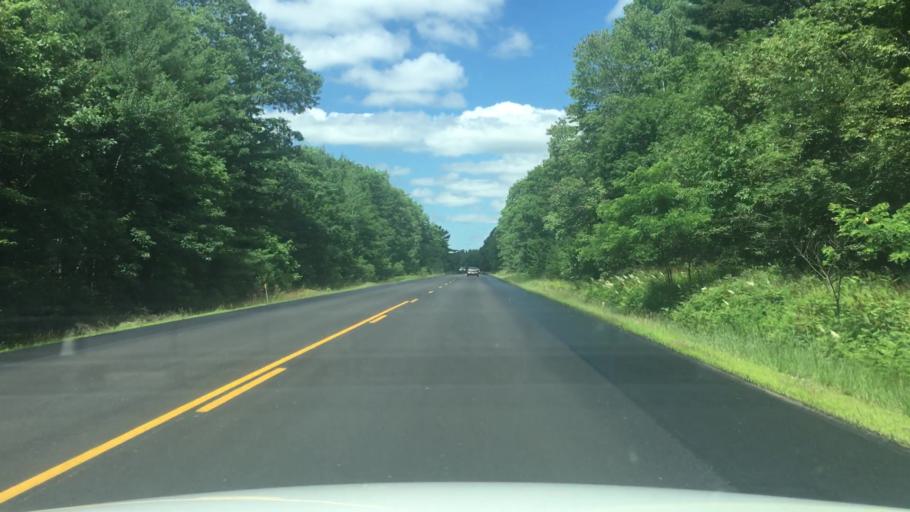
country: US
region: Maine
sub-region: Waldo County
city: Searsmont
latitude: 44.4060
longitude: -69.1701
